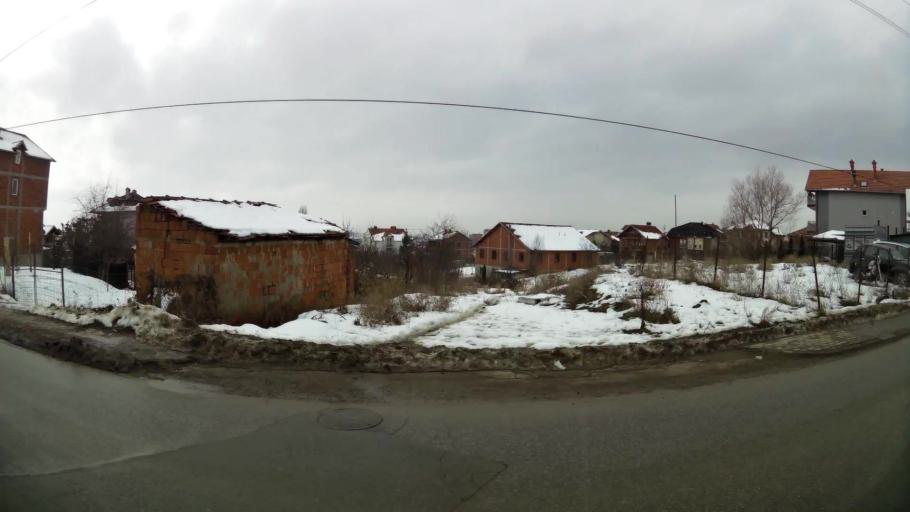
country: XK
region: Pristina
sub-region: Komuna e Prishtines
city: Pristina
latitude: 42.6517
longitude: 21.1932
